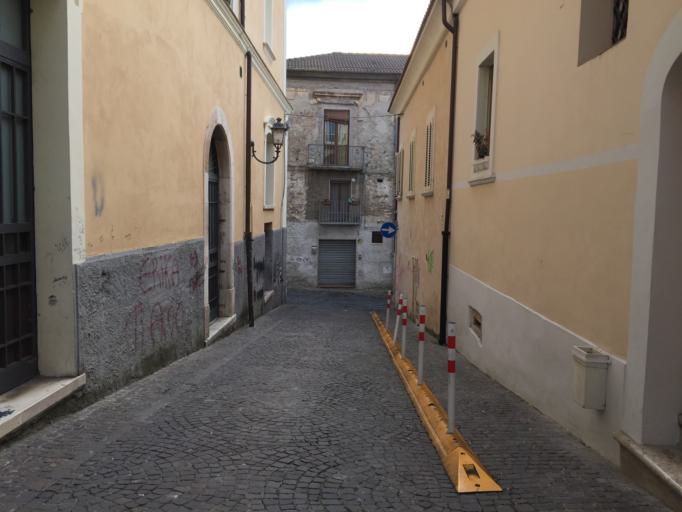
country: IT
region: Campania
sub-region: Provincia di Benevento
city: Benevento
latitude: 41.1302
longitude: 14.7770
